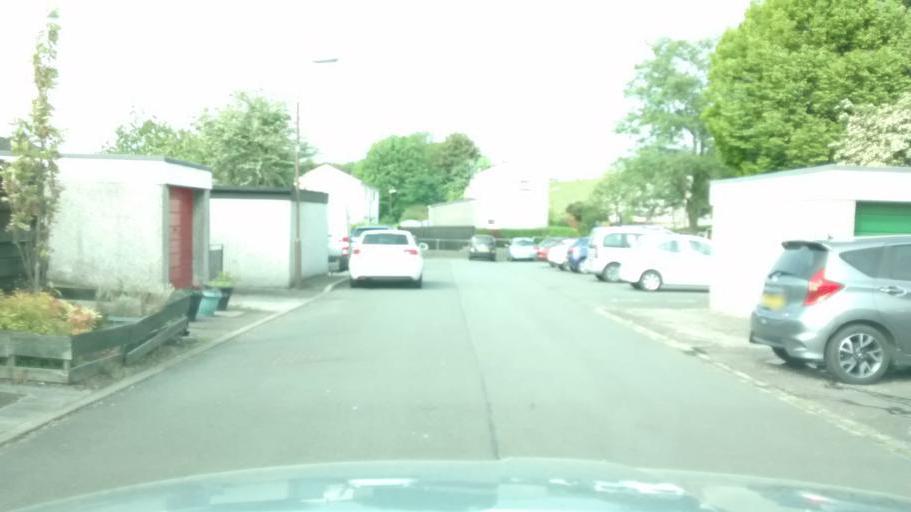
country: GB
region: Scotland
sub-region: West Lothian
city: Mid Calder
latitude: 55.8911
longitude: -3.4993
